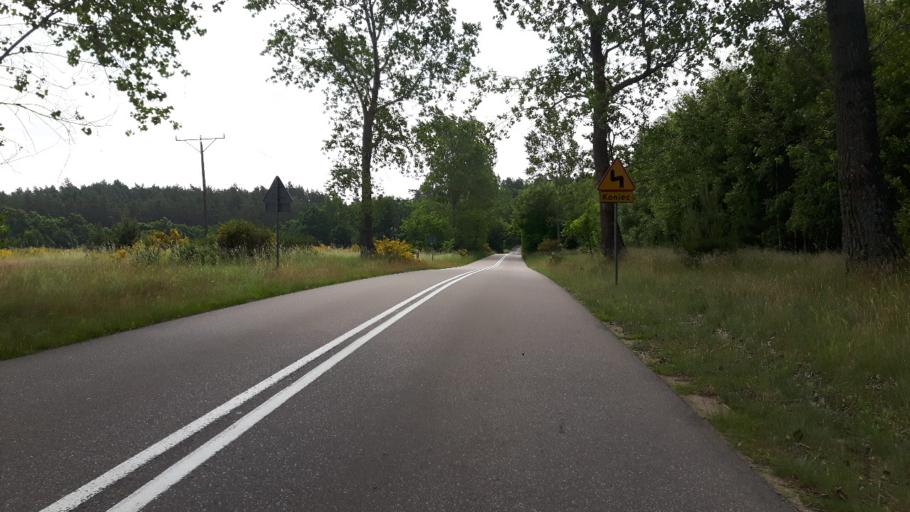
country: PL
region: Pomeranian Voivodeship
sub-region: Powiat leborski
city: Leba
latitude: 54.7530
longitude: 17.7102
